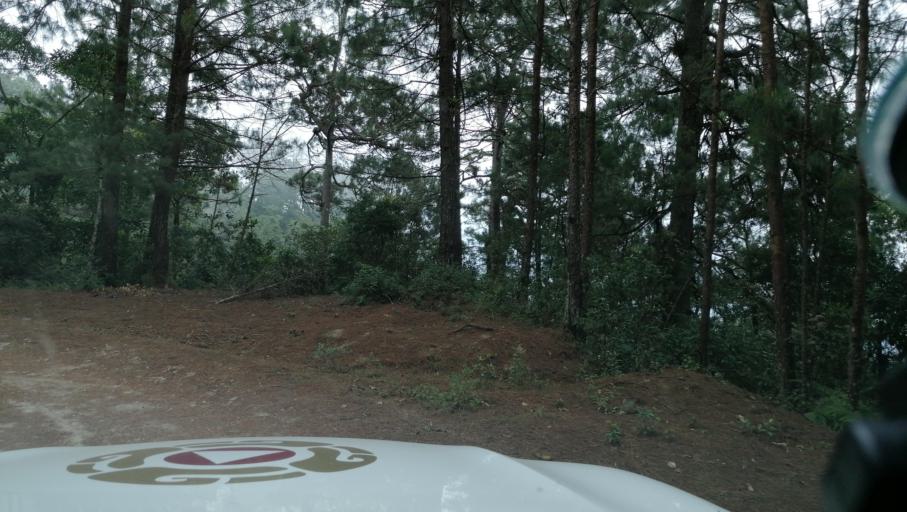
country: MX
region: Chiapas
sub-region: Tapachula
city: Canton Villaflor
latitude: 15.1983
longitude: -92.2320
